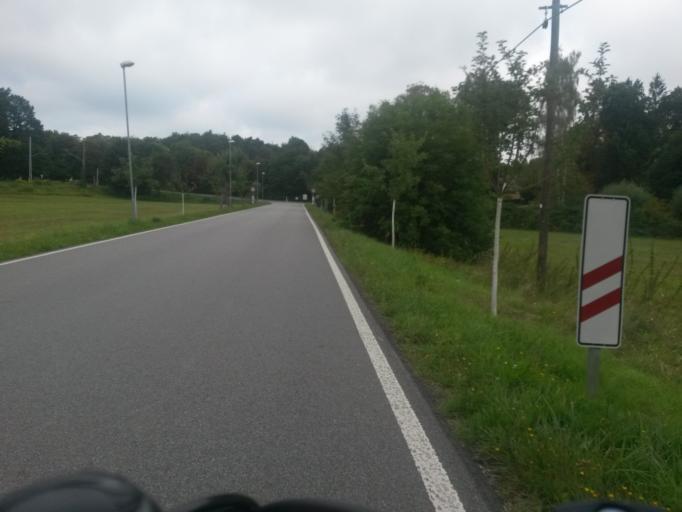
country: DE
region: Brandenburg
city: Angermunde
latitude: 53.0525
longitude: 13.9435
